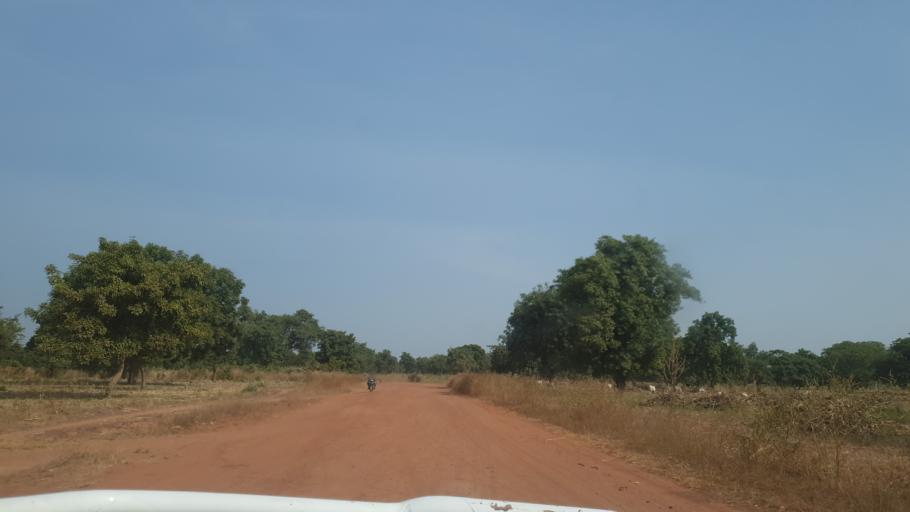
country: ML
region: Koulikoro
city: Dioila
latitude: 12.2281
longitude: -6.2183
